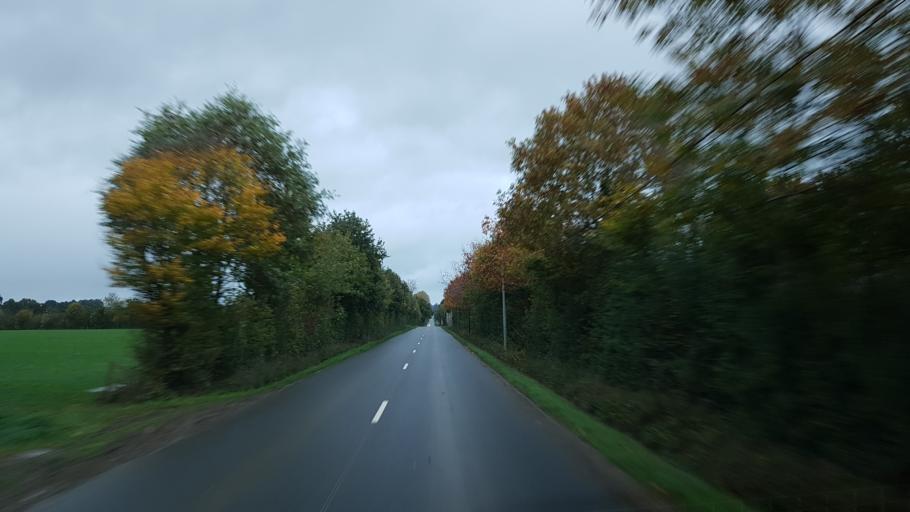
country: FR
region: Pays de la Loire
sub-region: Departement de la Mayenne
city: Juvigne
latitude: 48.1854
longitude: -1.1016
